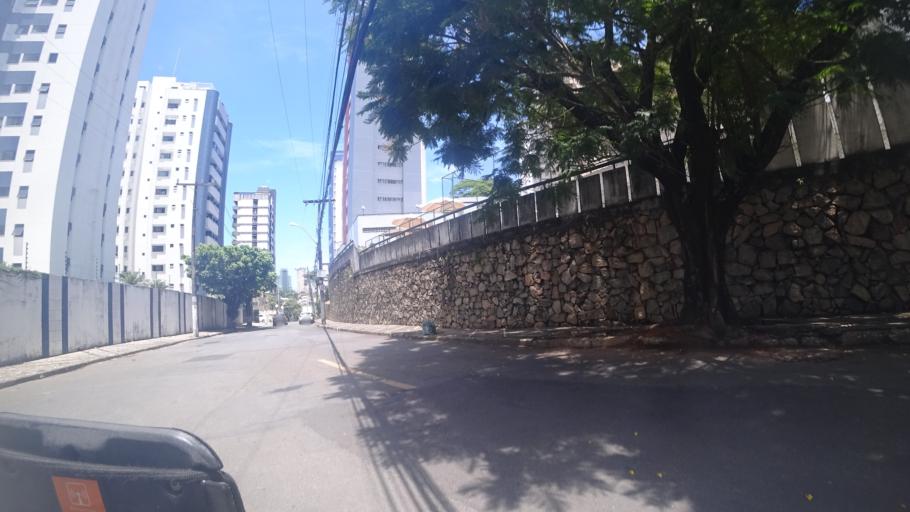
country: BR
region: Bahia
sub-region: Salvador
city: Salvador
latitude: -12.9857
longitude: -38.4626
